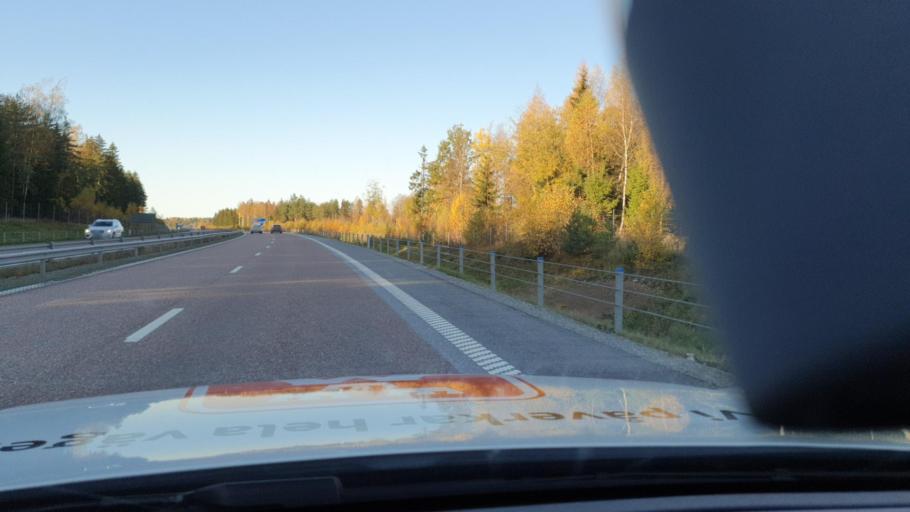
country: SE
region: Vaestmanland
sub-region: Vasteras
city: Tillberga
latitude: 59.6242
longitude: 16.6782
